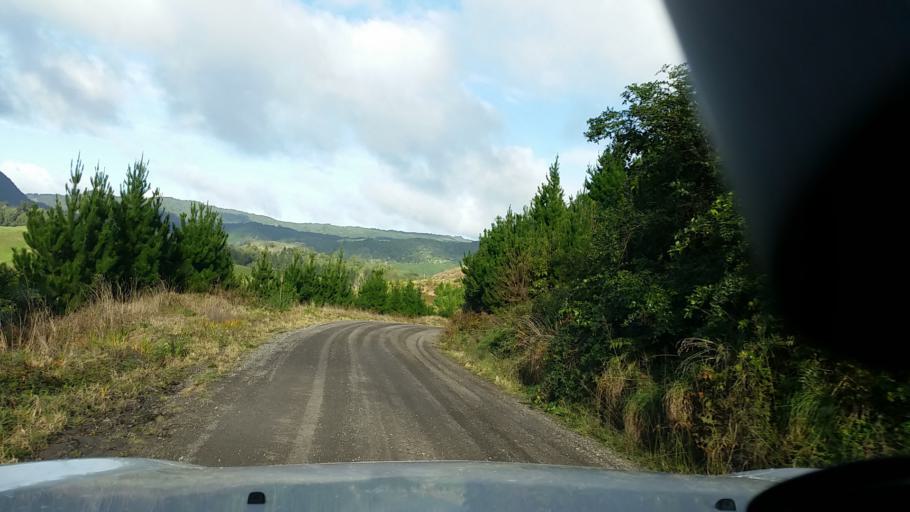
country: NZ
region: Bay of Plenty
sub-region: Kawerau District
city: Kawerau
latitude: -38.0321
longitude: 176.5535
